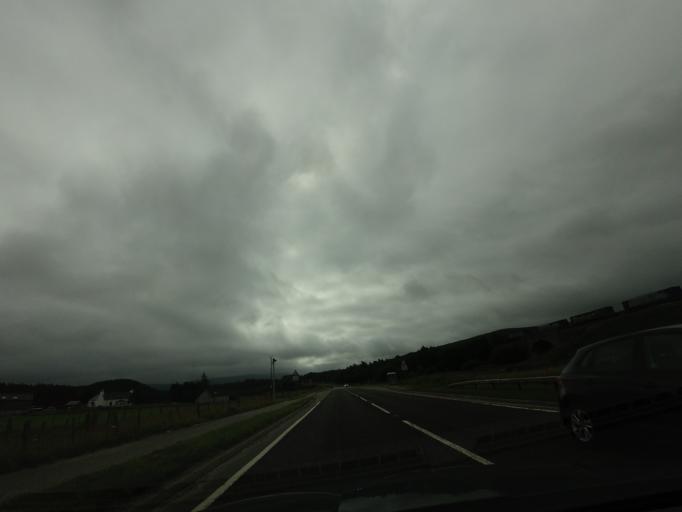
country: GB
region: Scotland
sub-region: Highland
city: Inverness
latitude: 57.3651
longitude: -4.0198
